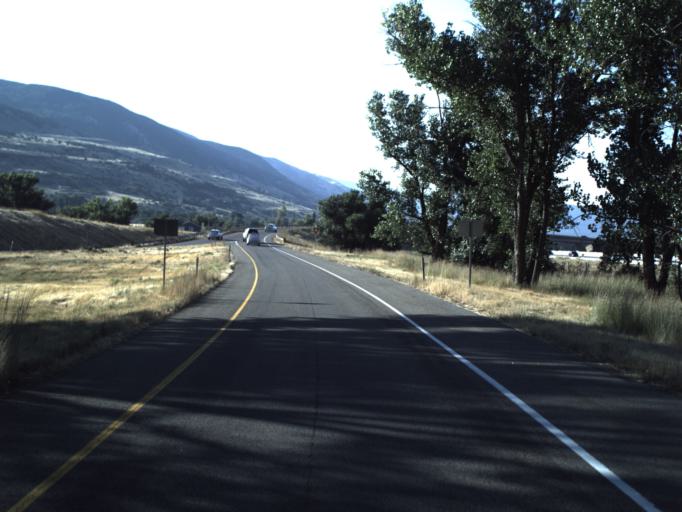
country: US
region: Utah
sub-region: Davis County
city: Farmington
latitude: 40.9735
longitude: -111.8936
